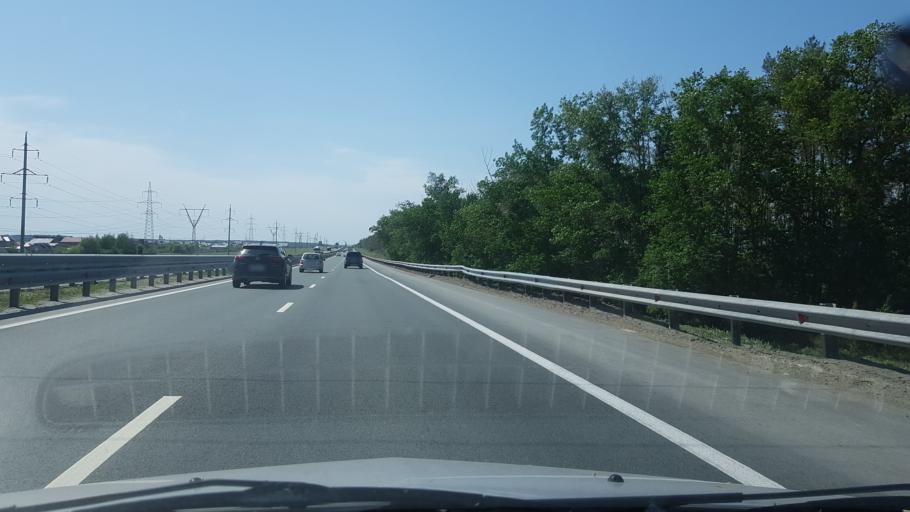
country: RU
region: Samara
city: Povolzhskiy
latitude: 53.5150
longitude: 49.6353
